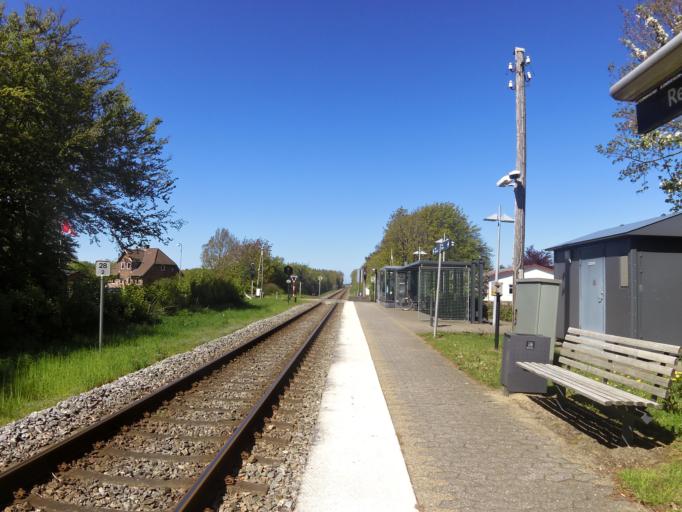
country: DK
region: South Denmark
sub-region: Tonder Kommune
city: Sherrebek
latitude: 55.2303
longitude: 8.7321
